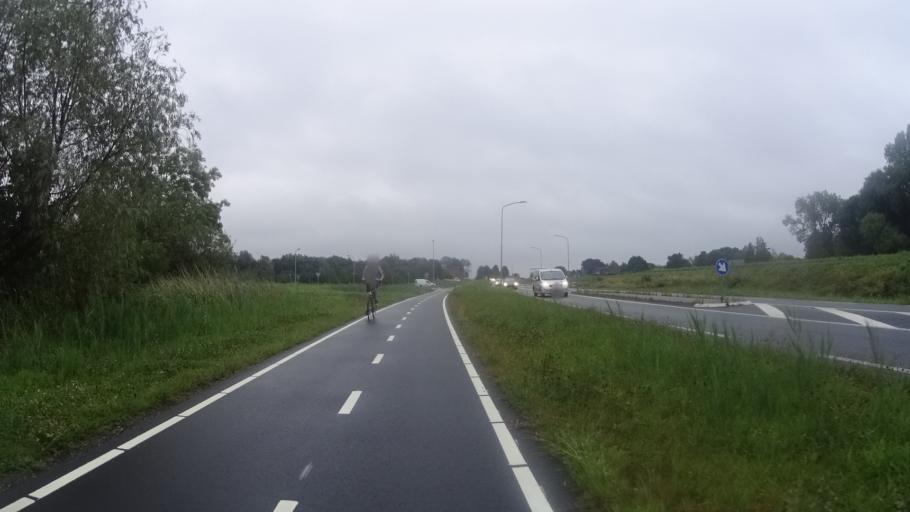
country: NL
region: Groningen
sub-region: Gemeente  Oldambt
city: Winschoten
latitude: 53.1628
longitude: 7.0166
